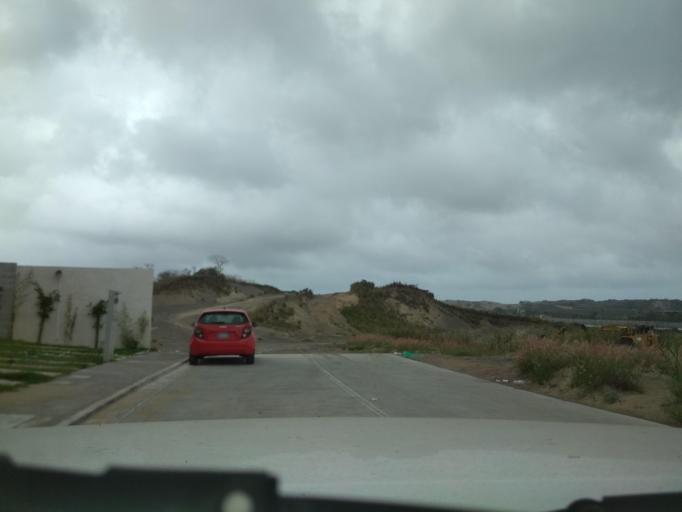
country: MX
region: Veracruz
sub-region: Veracruz
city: Fraccionamiento Geovillas los Pinos
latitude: 19.2188
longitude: -96.2336
